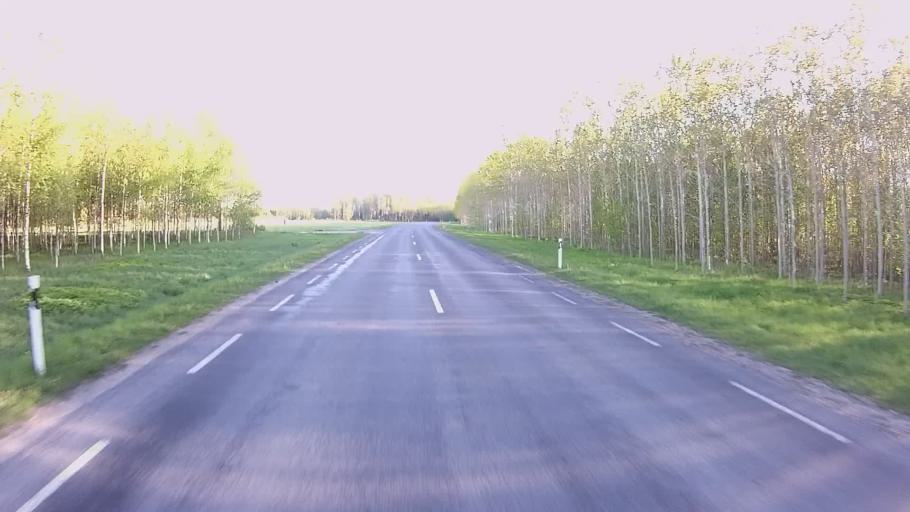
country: EE
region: Viljandimaa
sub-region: Viiratsi vald
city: Viiratsi
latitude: 58.4411
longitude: 25.7332
